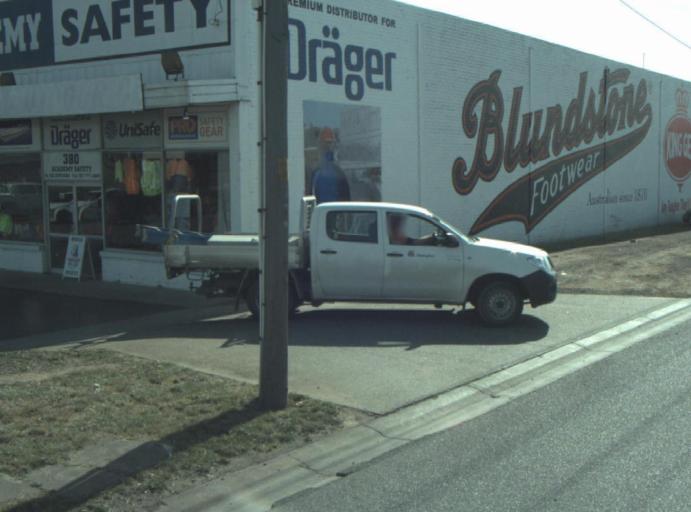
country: AU
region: Victoria
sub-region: Greater Geelong
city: Bell Park
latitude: -38.0998
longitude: 144.3457
